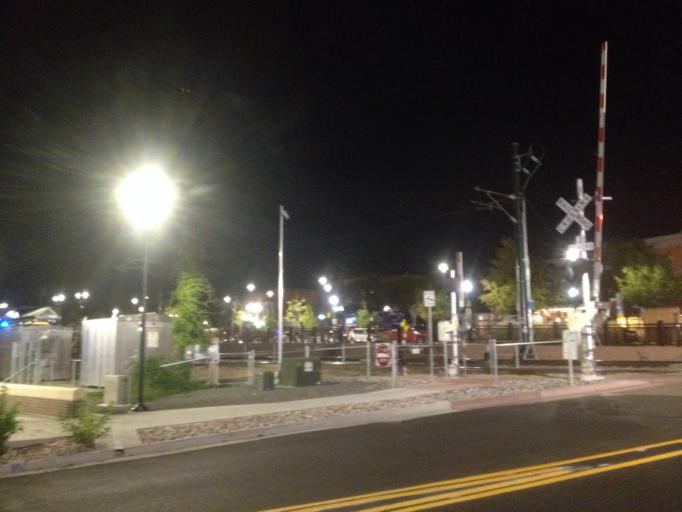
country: US
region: Colorado
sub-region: Jefferson County
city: Arvada
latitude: 39.7991
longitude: -105.0790
